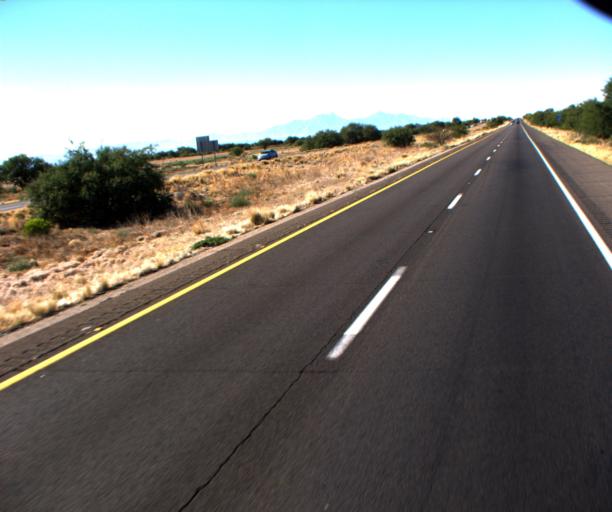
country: US
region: Arizona
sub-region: Pima County
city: Summit
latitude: 32.0975
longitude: -110.9936
